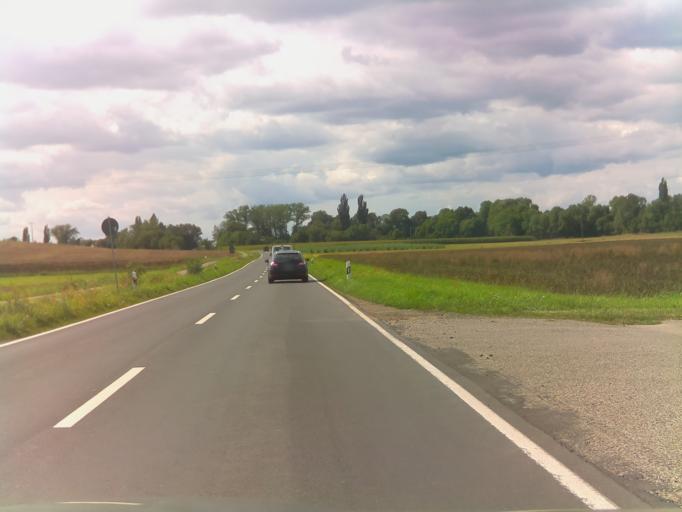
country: DE
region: Bavaria
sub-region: Regierungsbezirk Unterfranken
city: Sand
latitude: 49.9891
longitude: 10.5721
